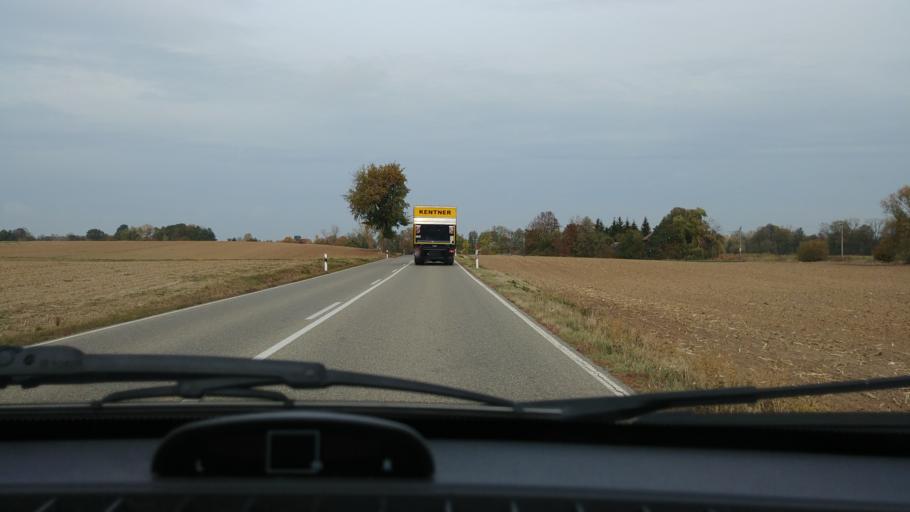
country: DE
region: Baden-Wuerttemberg
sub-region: Regierungsbezirk Stuttgart
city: Stimpfach
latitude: 49.0836
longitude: 10.0683
